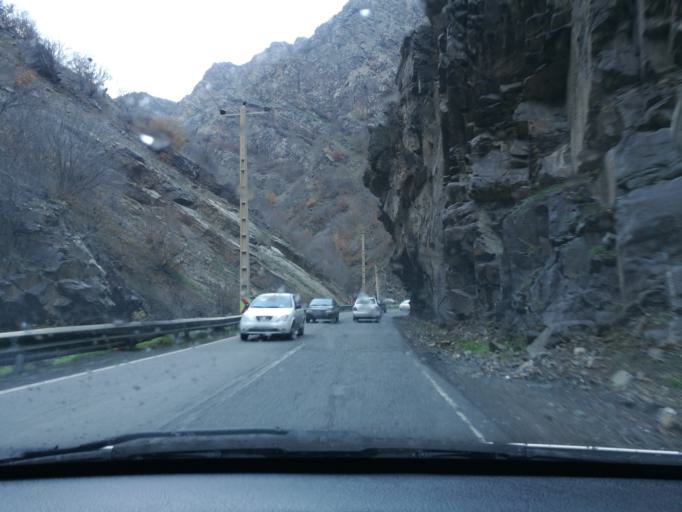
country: IR
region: Mazandaran
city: Chalus
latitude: 36.2843
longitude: 51.2422
